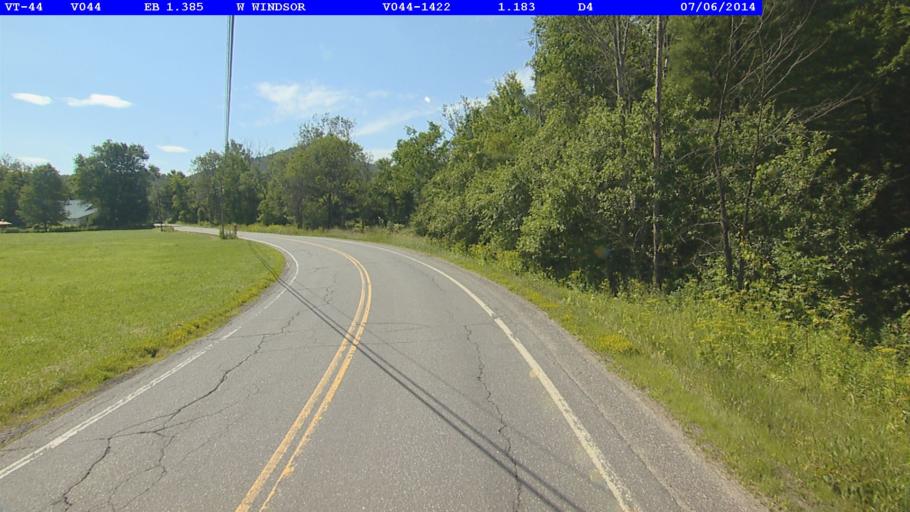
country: US
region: Vermont
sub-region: Windsor County
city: Windsor
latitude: 43.4570
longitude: -72.5179
